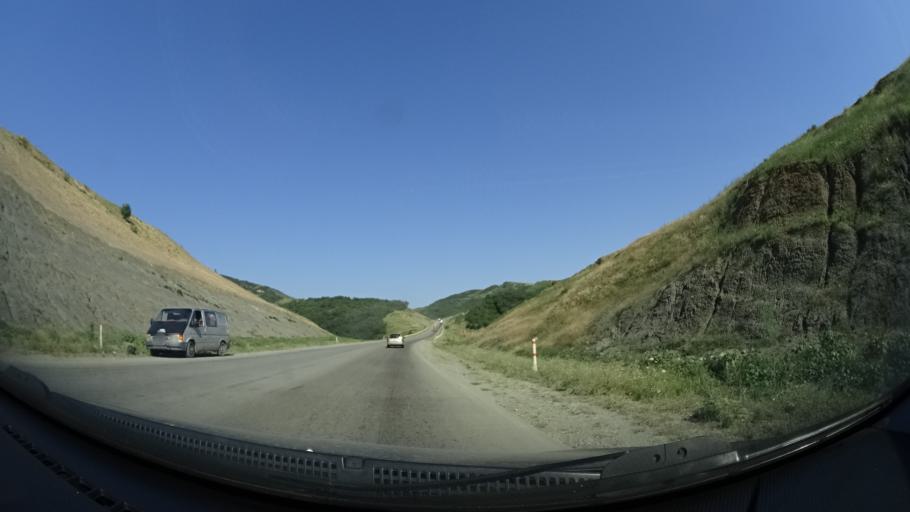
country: GE
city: Didi Lilo
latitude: 41.8018
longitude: 44.8922
